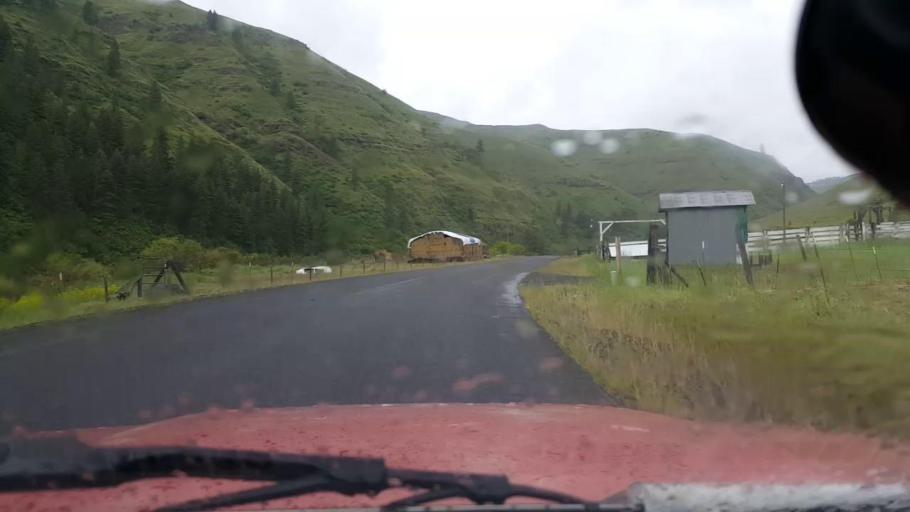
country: US
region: Washington
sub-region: Asotin County
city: Asotin
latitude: 46.0367
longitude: -117.2677
